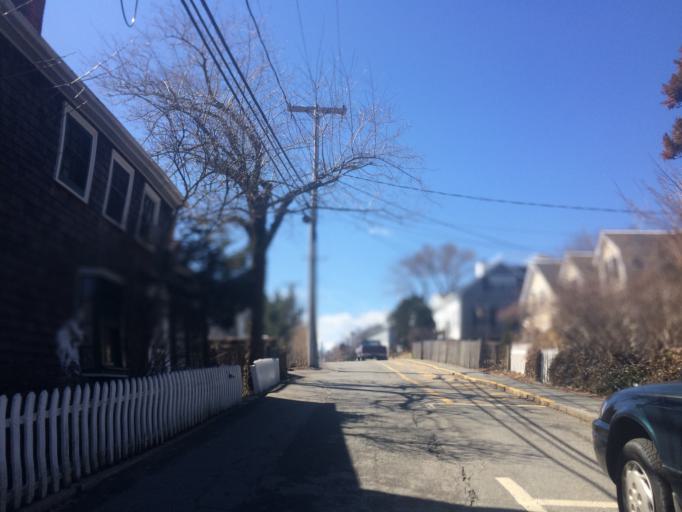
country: US
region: Massachusetts
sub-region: Barnstable County
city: Provincetown
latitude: 42.0407
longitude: -70.1947
